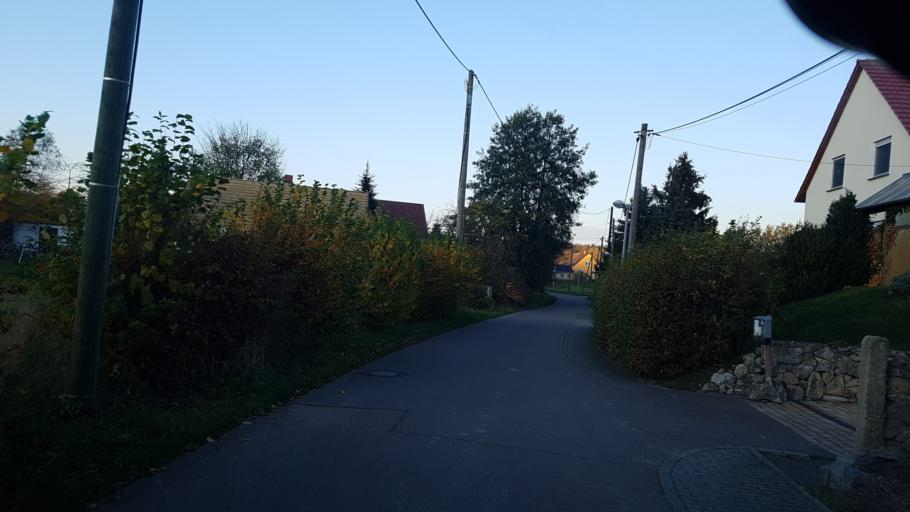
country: DE
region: Saxony
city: Schildau
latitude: 51.4262
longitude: 12.9744
